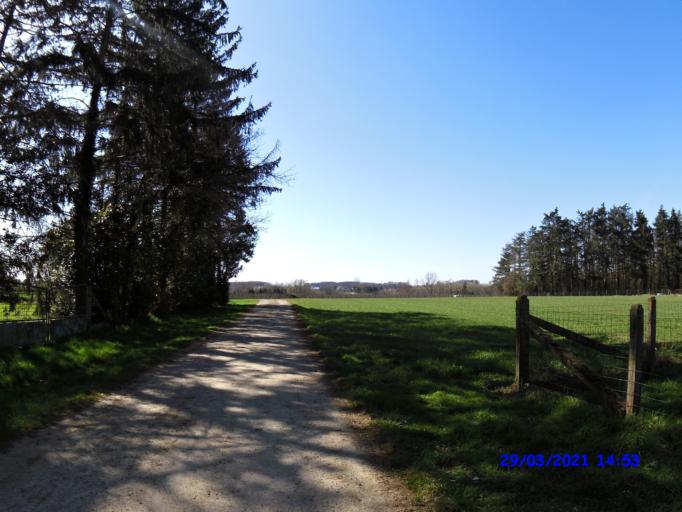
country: BE
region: Flanders
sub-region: Provincie Vlaams-Brabant
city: Lubbeek
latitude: 50.9093
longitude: 4.8589
